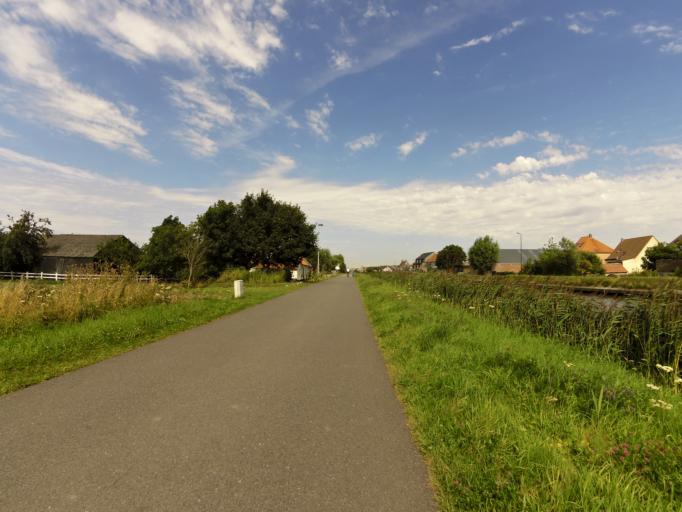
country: BE
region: Flanders
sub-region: Provincie West-Vlaanderen
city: Oudenburg
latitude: 51.1943
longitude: 3.0047
